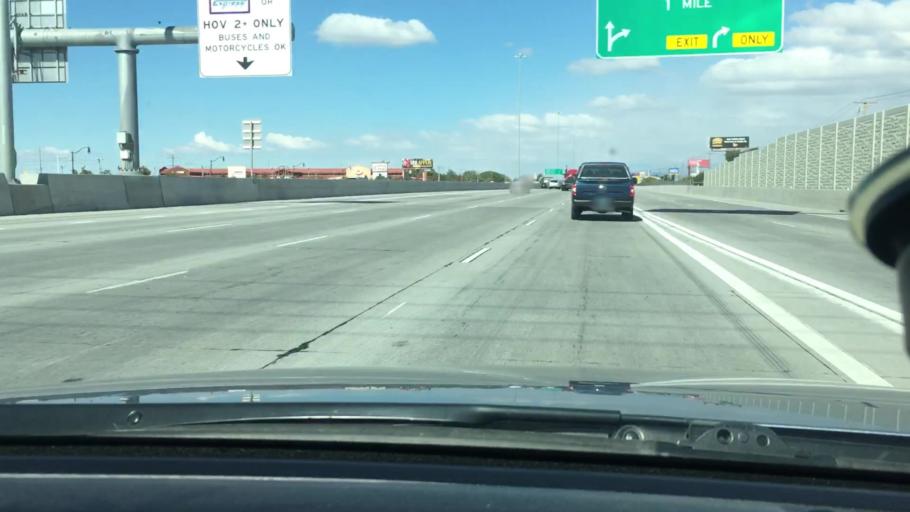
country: US
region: Utah
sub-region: Salt Lake County
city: Draper
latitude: 40.5081
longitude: -111.8909
